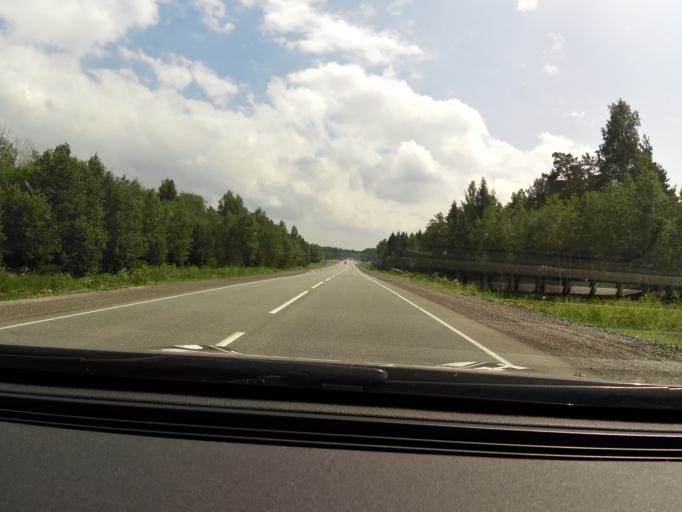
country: RU
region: Perm
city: Suksun
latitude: 57.0201
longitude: 57.4628
